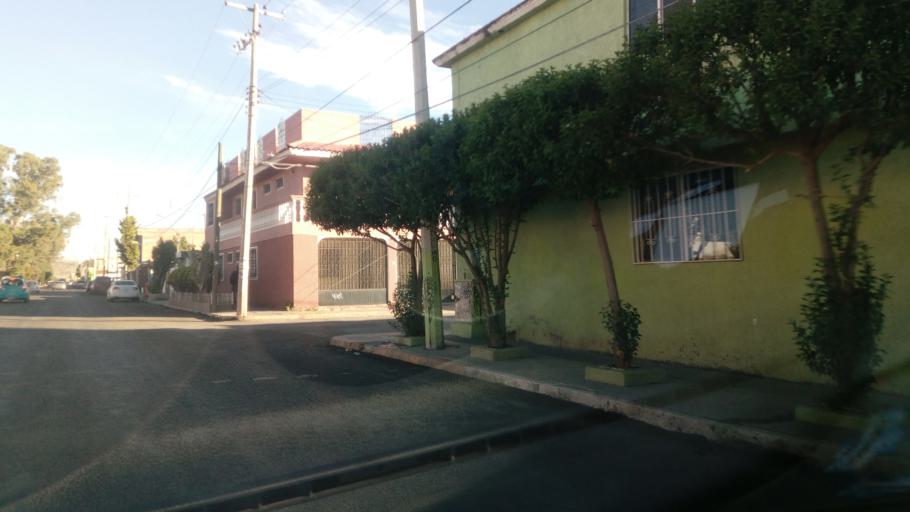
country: MX
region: Durango
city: Victoria de Durango
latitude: 24.0634
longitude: -104.5969
